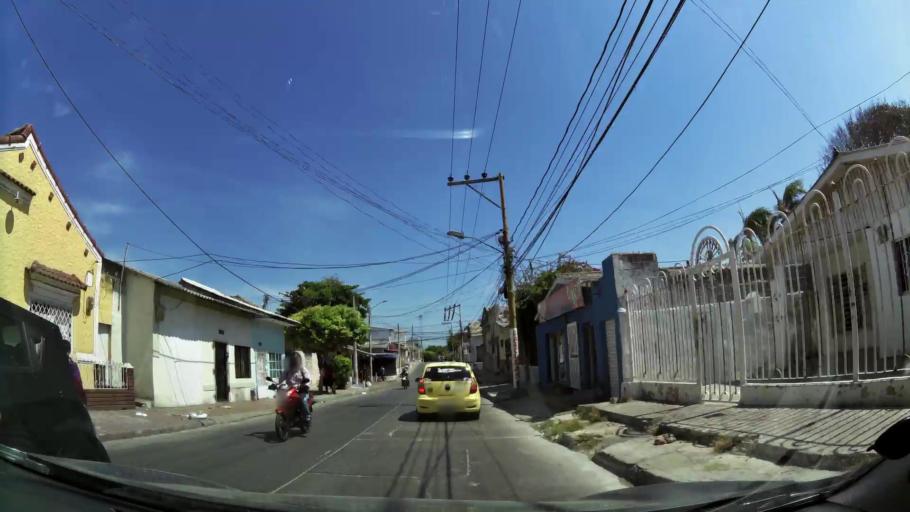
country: CO
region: Atlantico
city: Barranquilla
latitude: 10.9749
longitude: -74.7879
